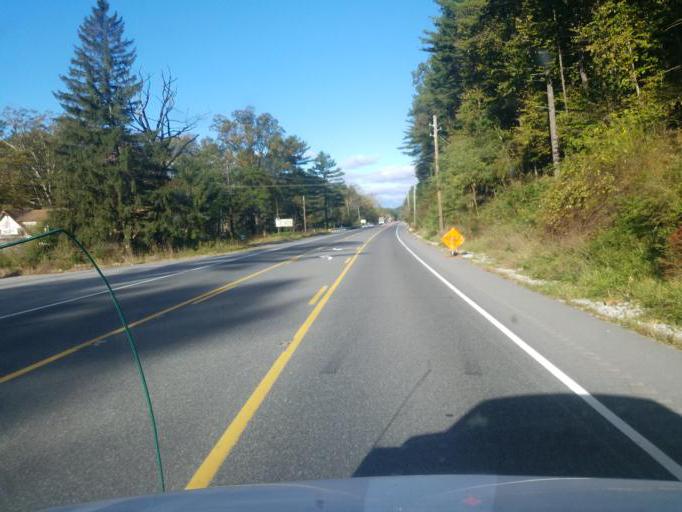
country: US
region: Pennsylvania
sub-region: Franklin County
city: Fayetteville
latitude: 39.9017
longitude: -77.4604
